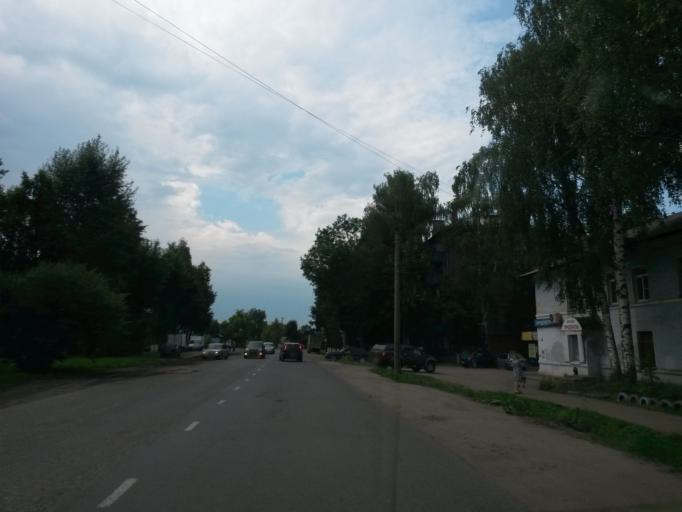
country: RU
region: Jaroslavl
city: Yaroslavl
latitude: 57.6065
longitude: 39.8145
